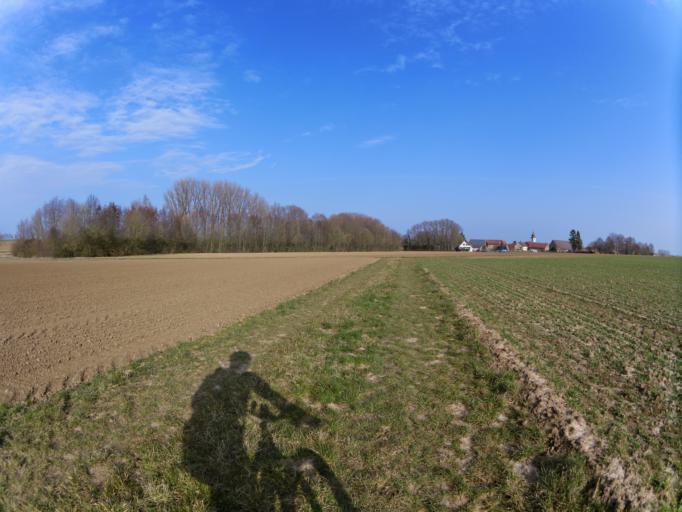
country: DE
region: Bavaria
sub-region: Regierungsbezirk Unterfranken
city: Sulzdorf
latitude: 49.6616
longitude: 9.9188
